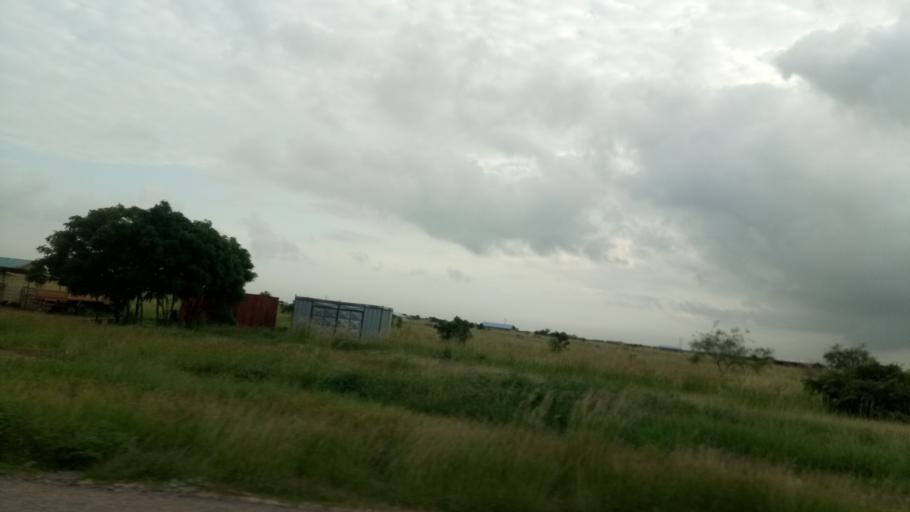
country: GH
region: Greater Accra
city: Tema
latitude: 5.8726
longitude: 0.3427
